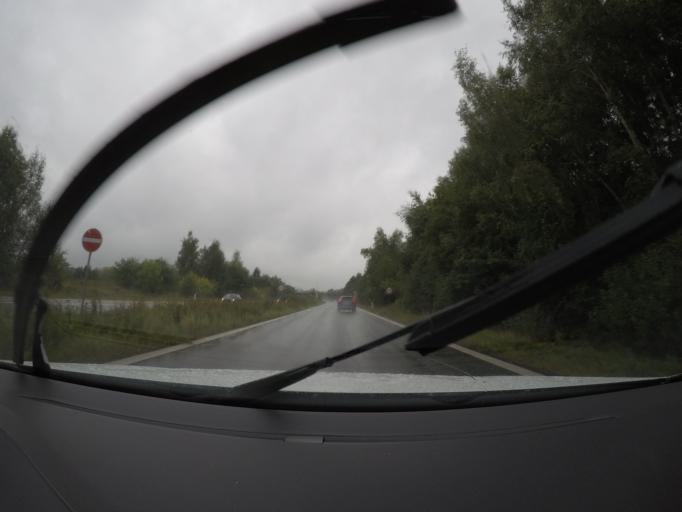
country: DK
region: Capital Region
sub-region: Helsingor Kommune
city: Espergaerde
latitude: 56.0059
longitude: 12.5326
